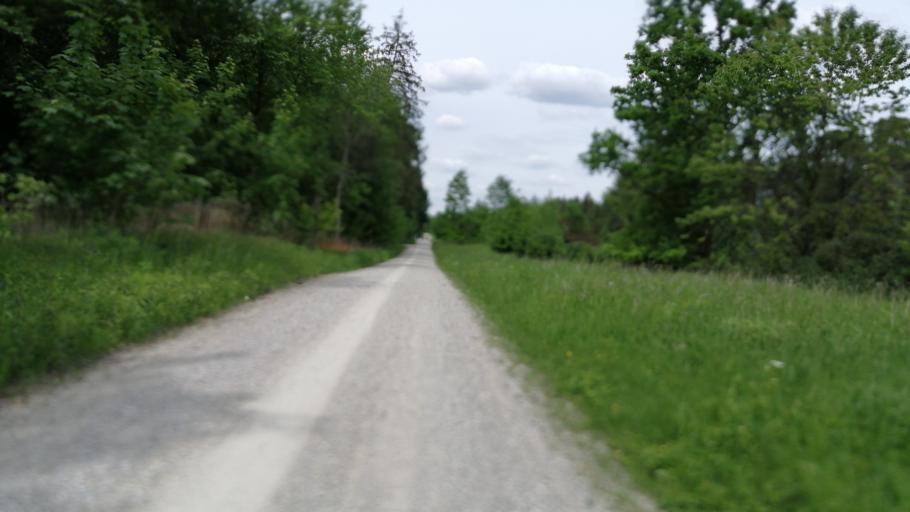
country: DE
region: Bavaria
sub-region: Upper Bavaria
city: Pullach im Isartal
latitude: 48.0583
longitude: 11.5648
